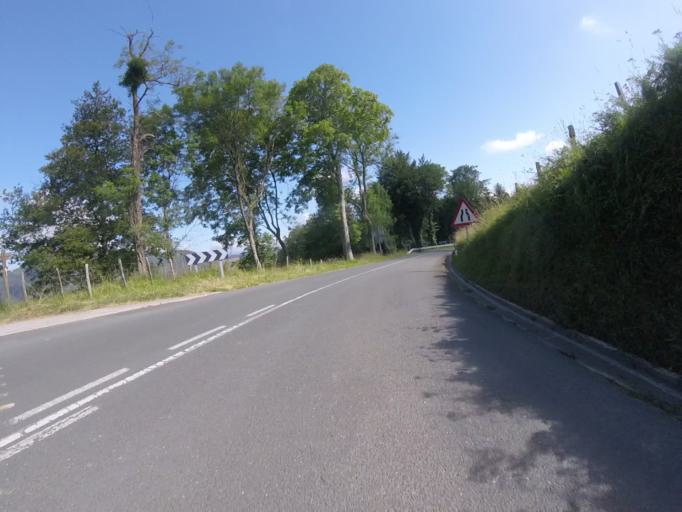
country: ES
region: Basque Country
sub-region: Provincia de Guipuzcoa
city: Ormaiztegui
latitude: 43.0878
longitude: -2.2457
